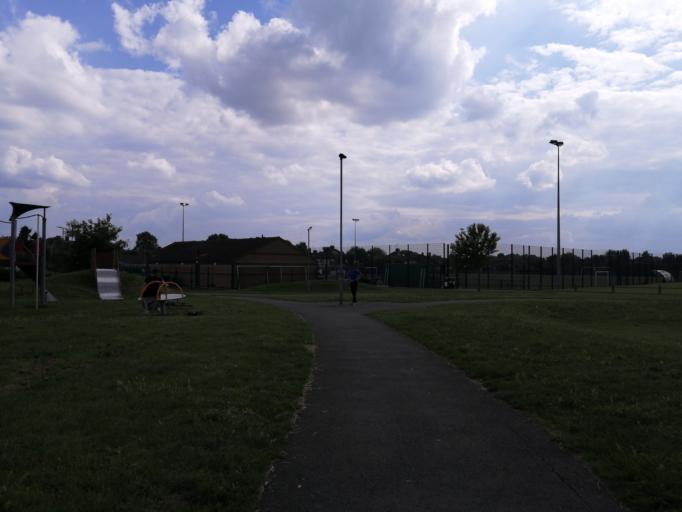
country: GB
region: England
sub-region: Peterborough
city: Peterborough
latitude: 52.5798
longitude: -0.2666
